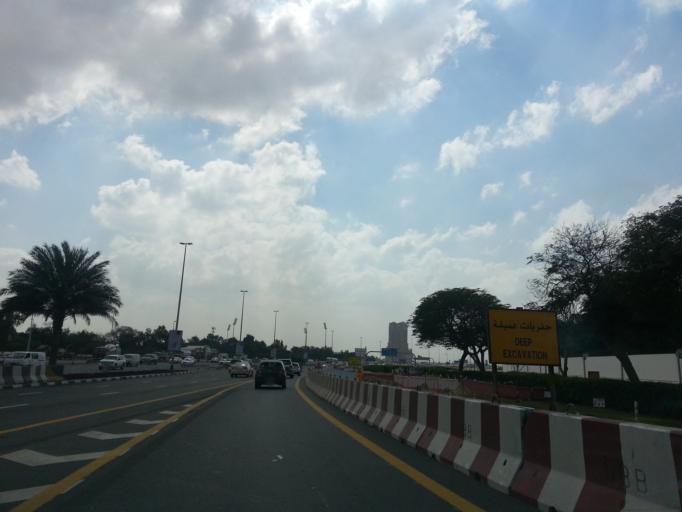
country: AE
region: Ash Shariqah
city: Sharjah
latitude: 25.2260
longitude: 55.3151
